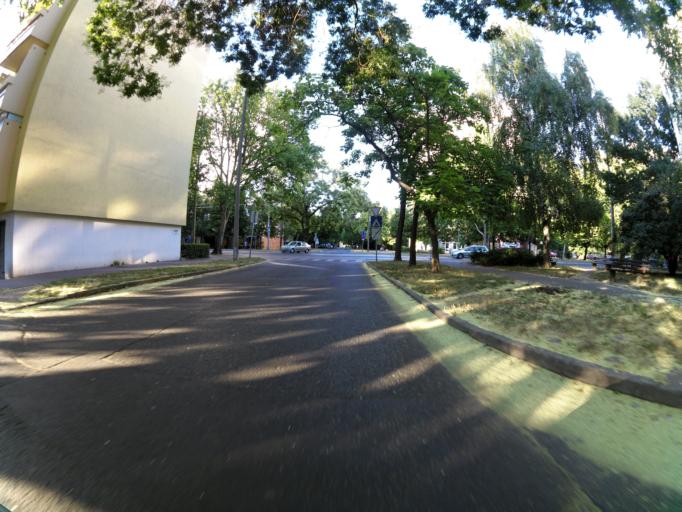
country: HU
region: Csongrad
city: Szeged
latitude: 46.2637
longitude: 20.1691
